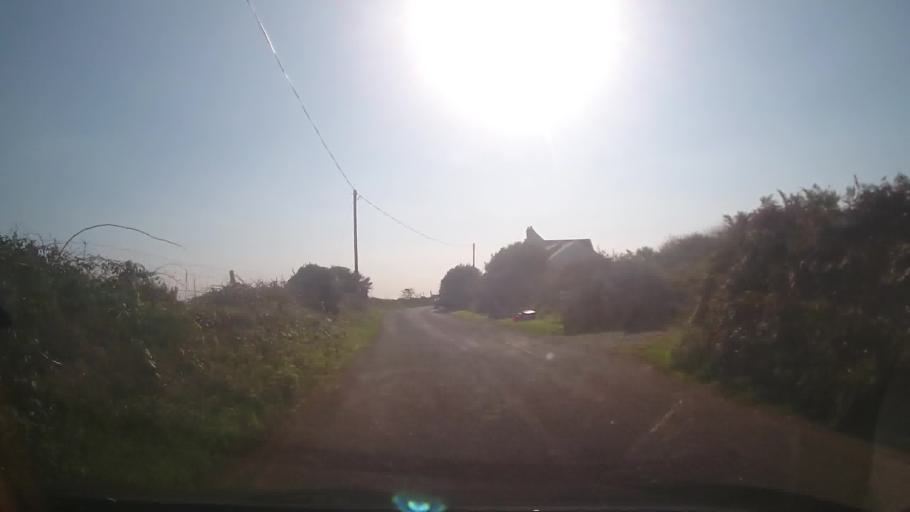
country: GB
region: Wales
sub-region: Pembrokeshire
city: Saint David's
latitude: 51.9172
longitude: -5.2351
